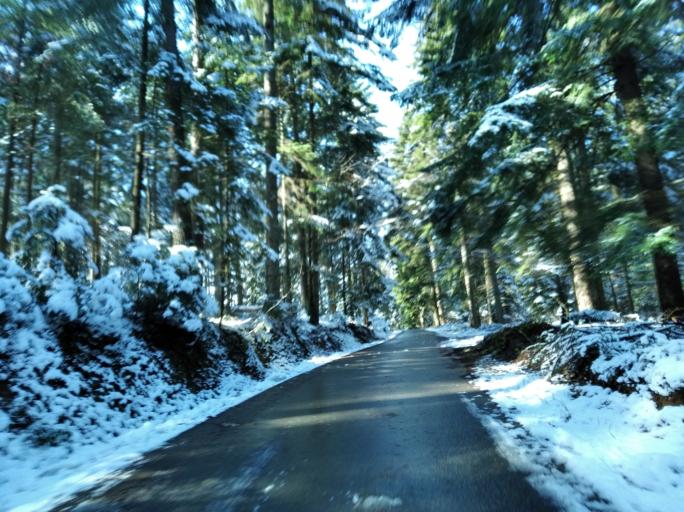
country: PL
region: Subcarpathian Voivodeship
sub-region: Powiat krosnienski
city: Korczyna
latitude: 49.7425
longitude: 21.8275
